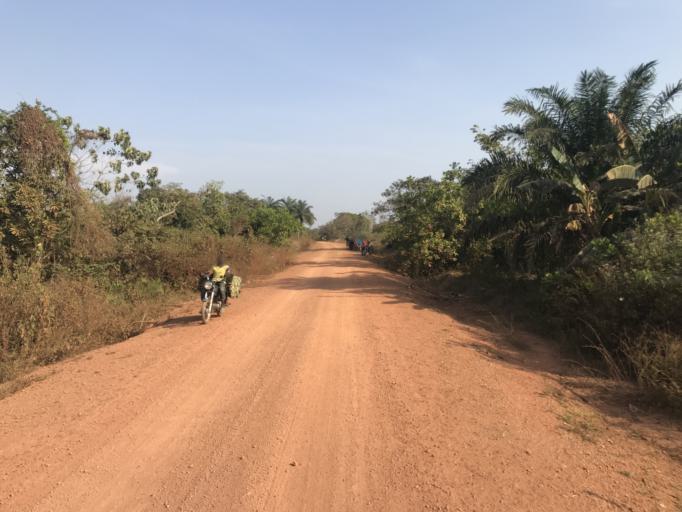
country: NG
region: Osun
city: Inisa
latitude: 7.7988
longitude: 4.2863
